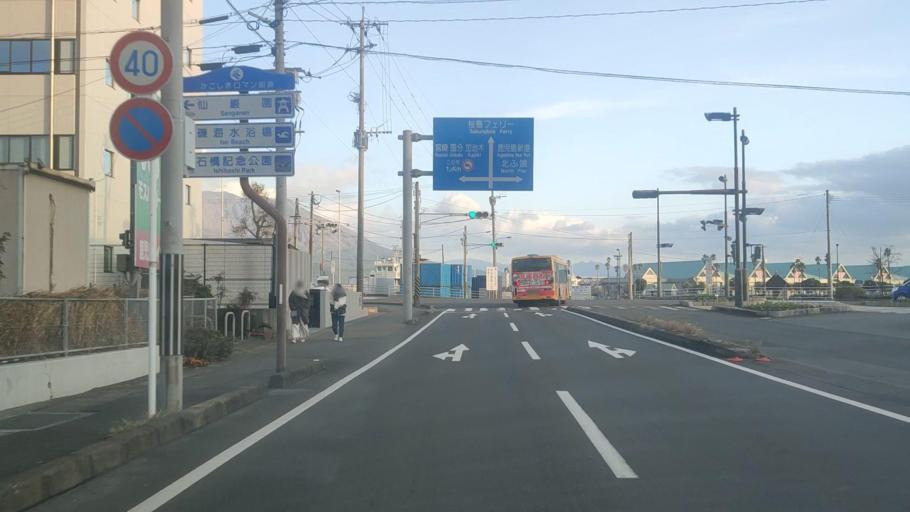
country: JP
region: Kagoshima
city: Kagoshima-shi
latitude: 31.5992
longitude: 130.5636
